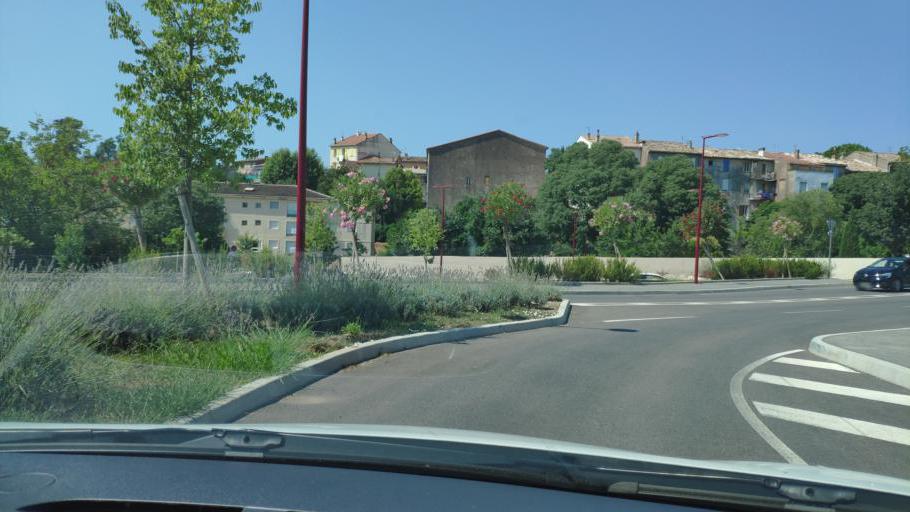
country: FR
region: Provence-Alpes-Cote d'Azur
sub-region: Departement du Var
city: Les Arcs
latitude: 43.4617
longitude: 6.4821
